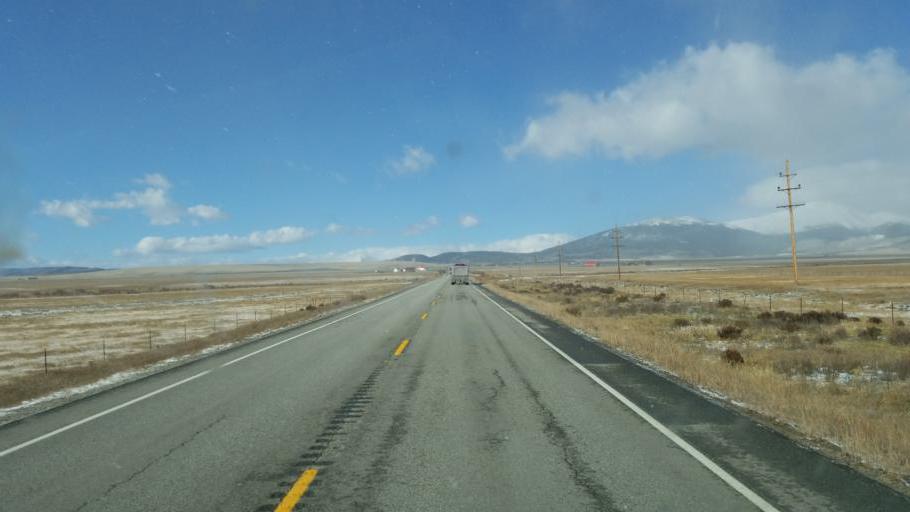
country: US
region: Colorado
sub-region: Park County
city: Fairplay
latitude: 39.3529
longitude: -105.8273
